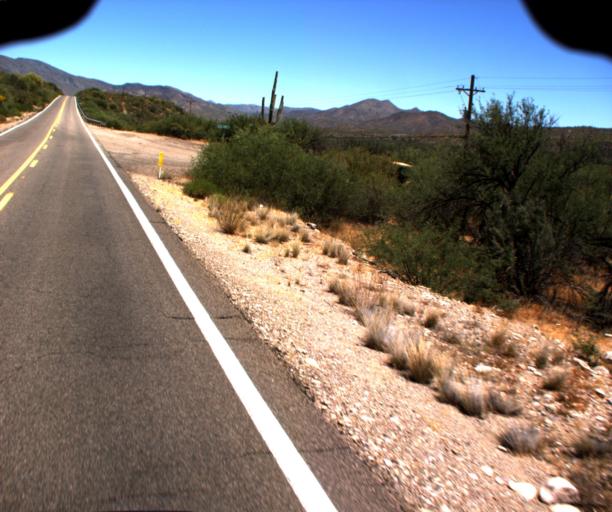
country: US
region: Arizona
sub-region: Pinal County
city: Kearny
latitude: 33.1017
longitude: -110.7436
